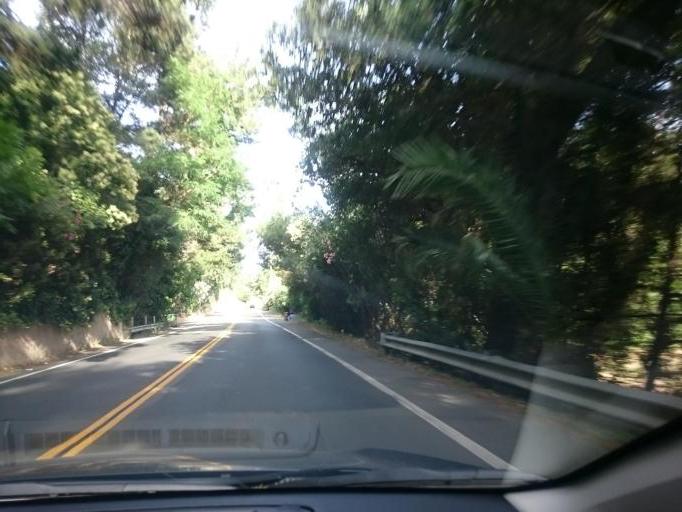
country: US
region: California
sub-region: Napa County
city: Saint Helena
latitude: 38.5099
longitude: -122.4503
